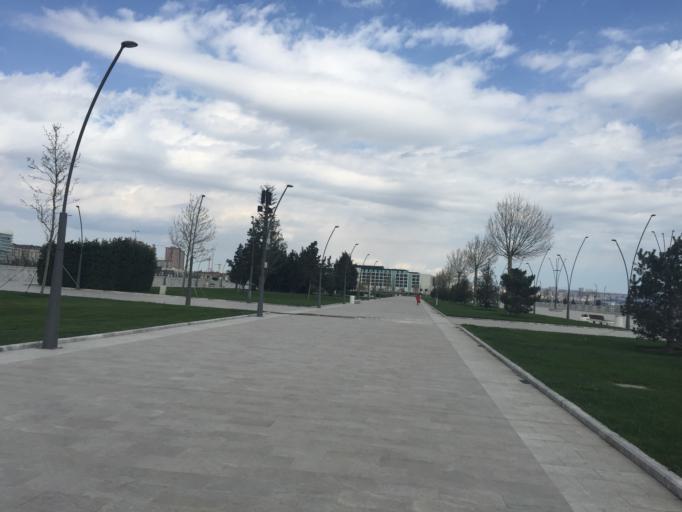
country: AZ
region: Baki
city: Baku
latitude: 40.3751
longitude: 49.8755
